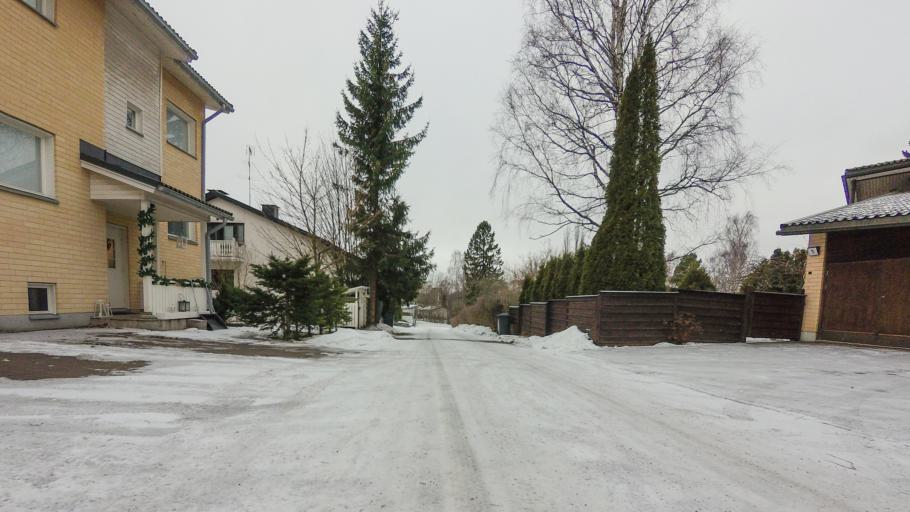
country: FI
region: Uusimaa
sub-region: Helsinki
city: Vantaa
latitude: 60.1910
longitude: 25.0572
